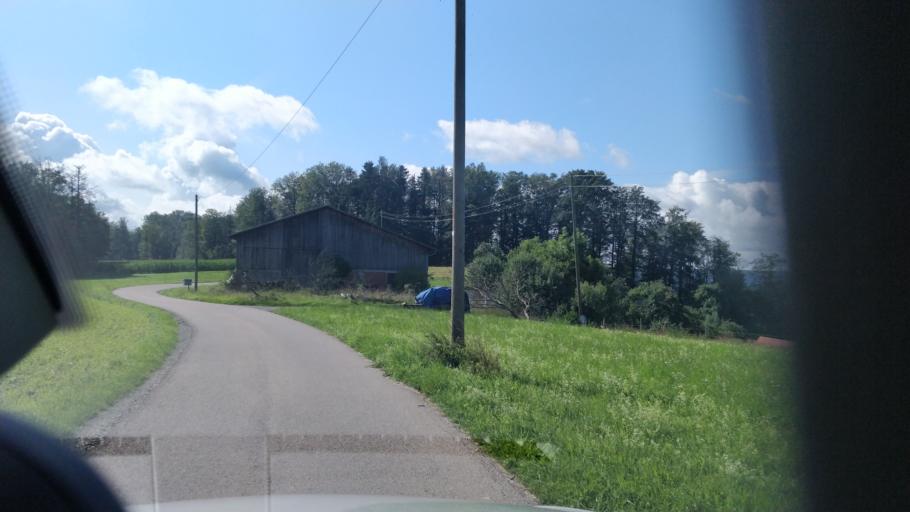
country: DE
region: Baden-Wuerttemberg
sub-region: Regierungsbezirk Stuttgart
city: Oberrot
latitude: 48.9976
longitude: 9.6529
